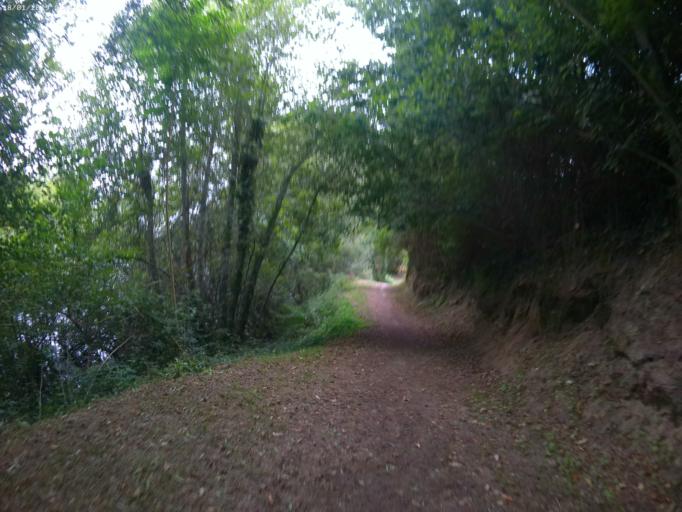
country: PT
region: Viana do Castelo
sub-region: Ponte da Barca
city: Ponte da Barca
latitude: 41.8066
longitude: -8.4462
